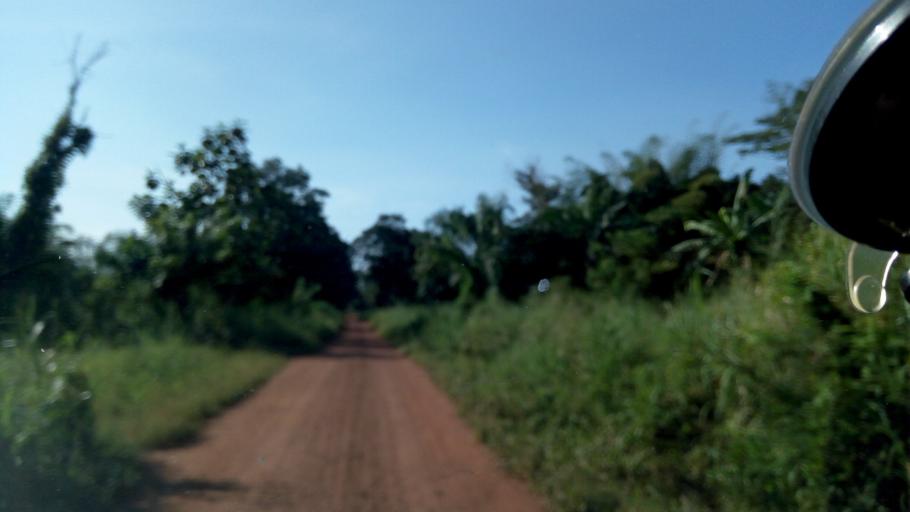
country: CF
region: Bangui
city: Bangui
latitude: 4.0409
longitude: 18.7478
